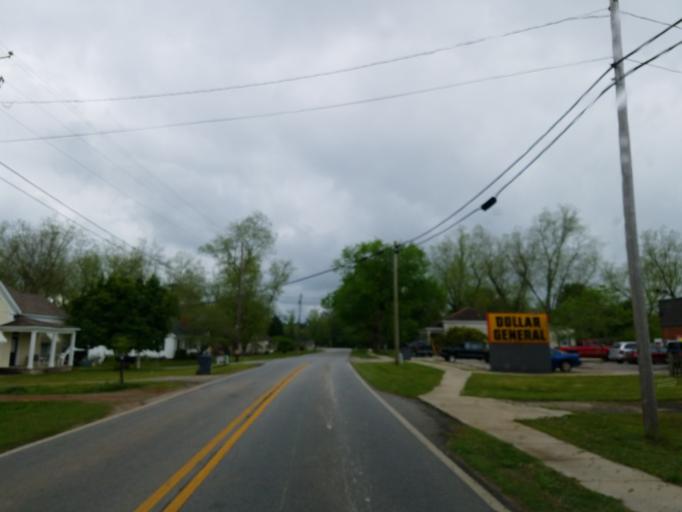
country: US
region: Georgia
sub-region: Lamar County
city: Barnesville
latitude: 33.1130
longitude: -84.1959
